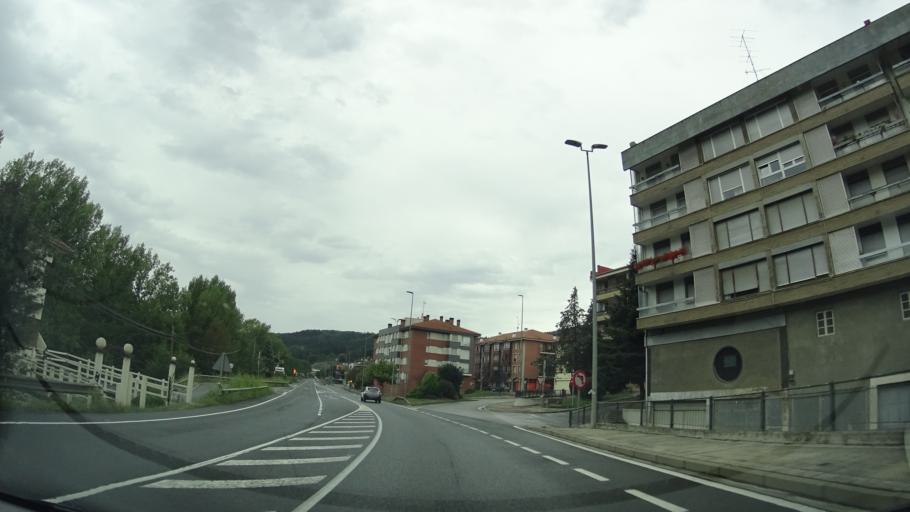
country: ES
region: Basque Country
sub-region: Bizkaia
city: Amorebieta
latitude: 43.2085
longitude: -2.7792
